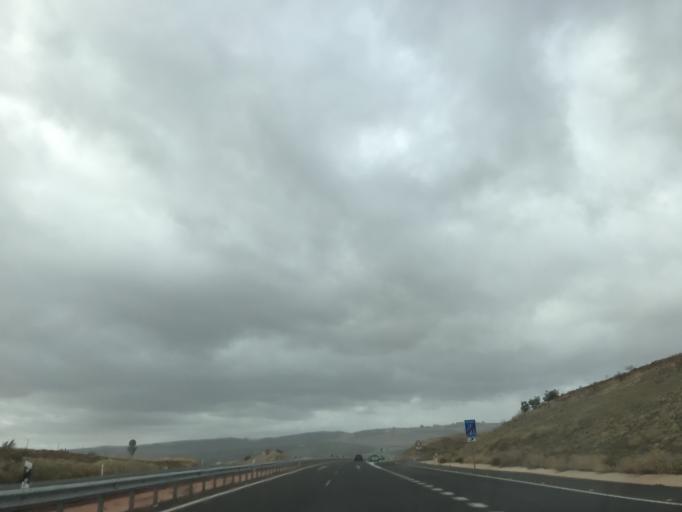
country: ES
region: Andalusia
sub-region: Provincia de Jaen
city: Lupion
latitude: 38.0692
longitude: -3.5654
